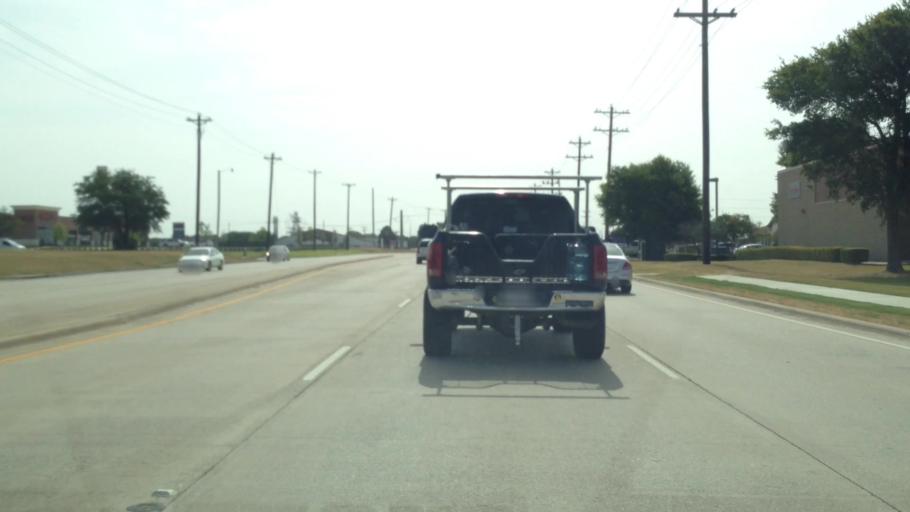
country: US
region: Texas
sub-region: Denton County
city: Lewisville
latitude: 33.0057
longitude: -97.0151
